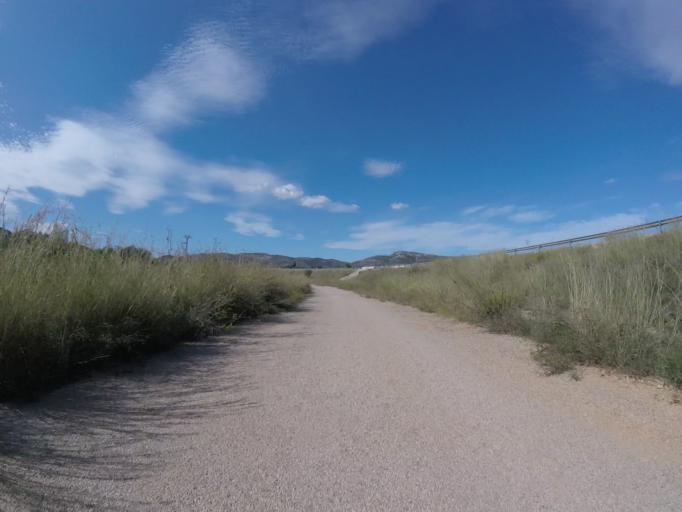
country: ES
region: Valencia
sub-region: Provincia de Castello
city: Peniscola
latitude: 40.3957
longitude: 0.3655
